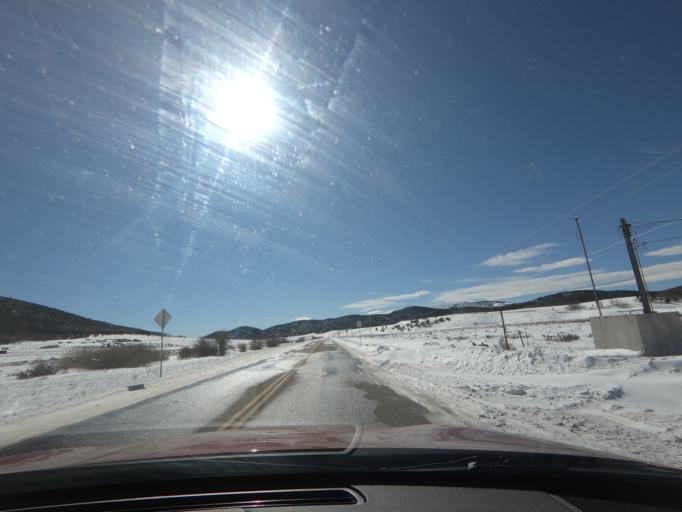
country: US
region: Colorado
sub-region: Teller County
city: Cripple Creek
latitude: 38.7804
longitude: -105.1224
